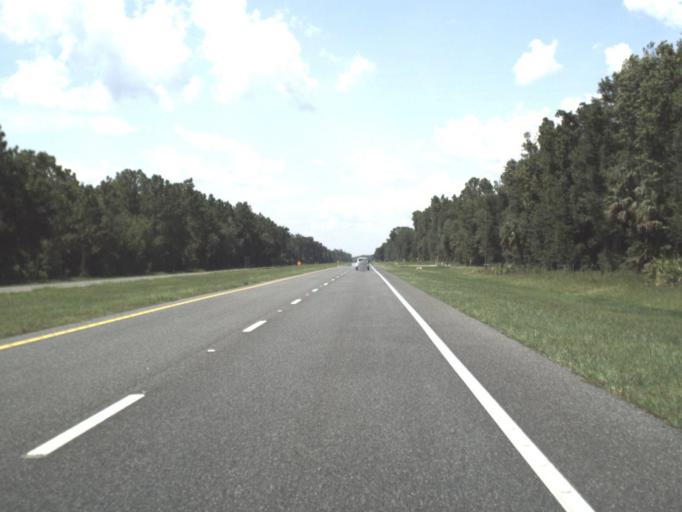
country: US
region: Florida
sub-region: Levy County
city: Inglis
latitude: 29.1047
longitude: -82.6361
